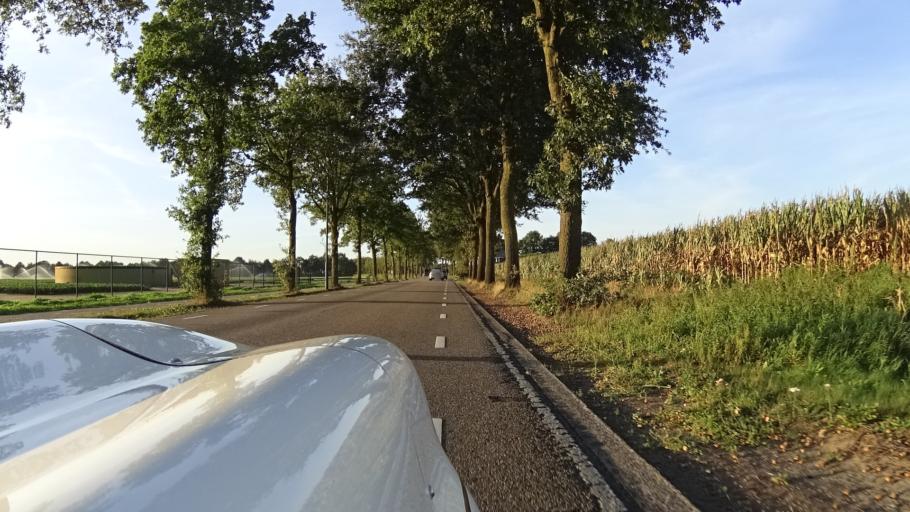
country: NL
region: North Brabant
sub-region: Gemeente Veghel
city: Erp
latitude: 51.6141
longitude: 5.6108
